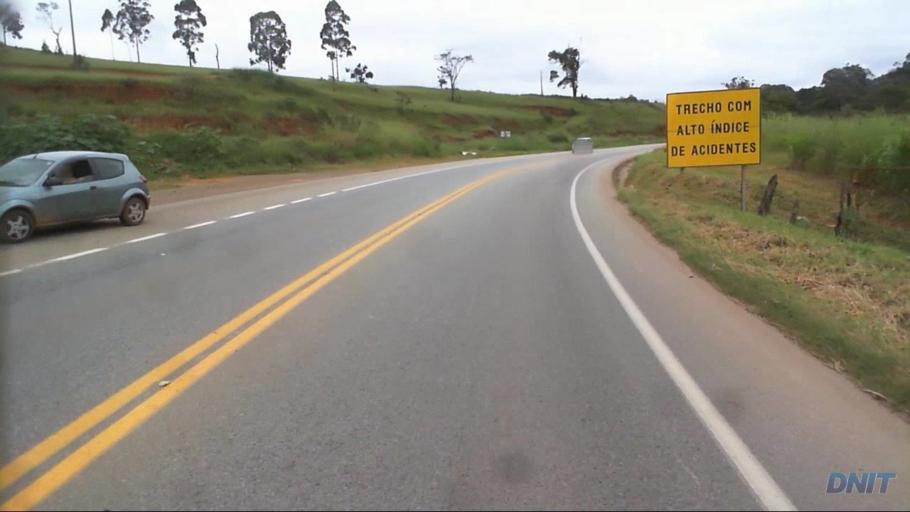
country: BR
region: Minas Gerais
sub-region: Joao Monlevade
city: Joao Monlevade
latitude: -19.8495
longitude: -43.2078
